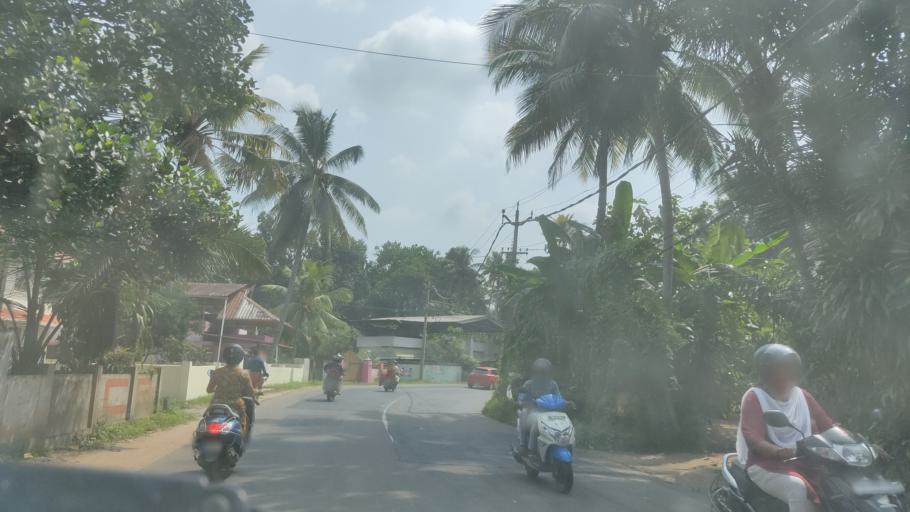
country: IN
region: Kerala
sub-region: Pattanamtitta
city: Tiruvalla
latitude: 9.3349
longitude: 76.5345
